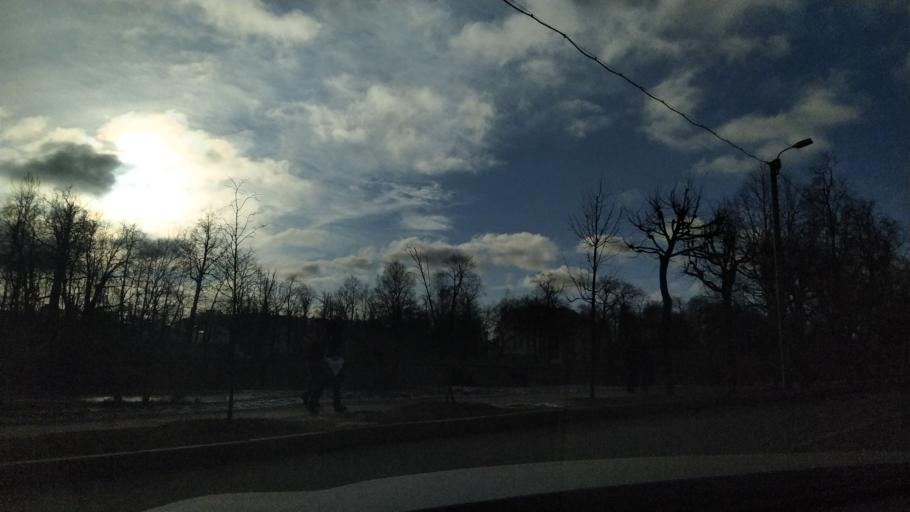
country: RU
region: St.-Petersburg
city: Pushkin
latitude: 59.7152
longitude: 30.4125
